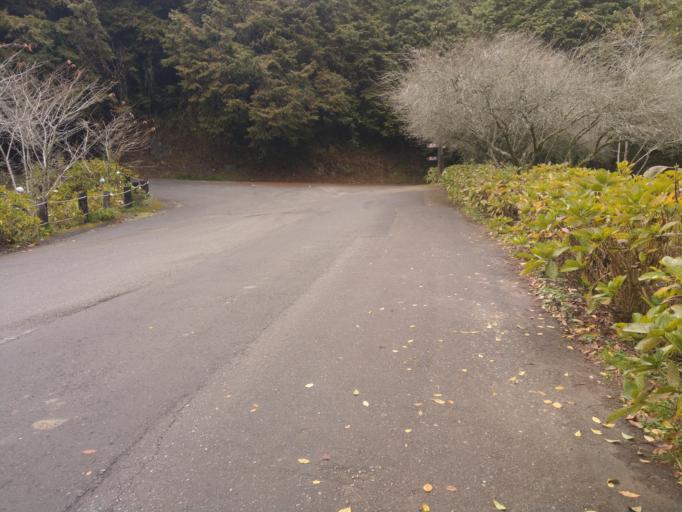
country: TW
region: Taiwan
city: Lugu
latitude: 23.6284
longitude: 120.7985
